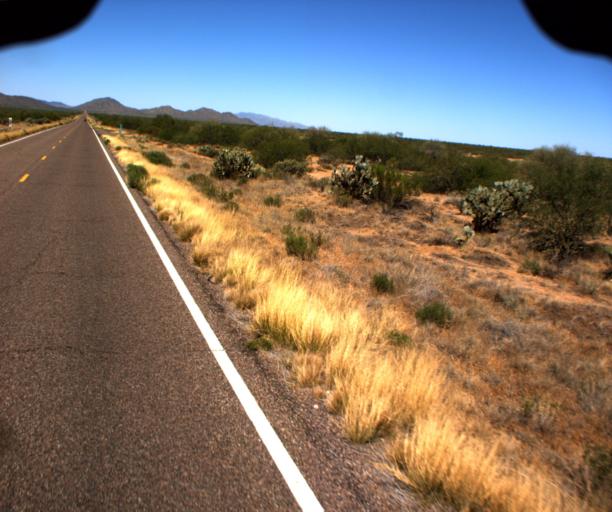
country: US
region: Arizona
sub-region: Yavapai County
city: Congress
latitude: 34.1368
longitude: -112.9170
